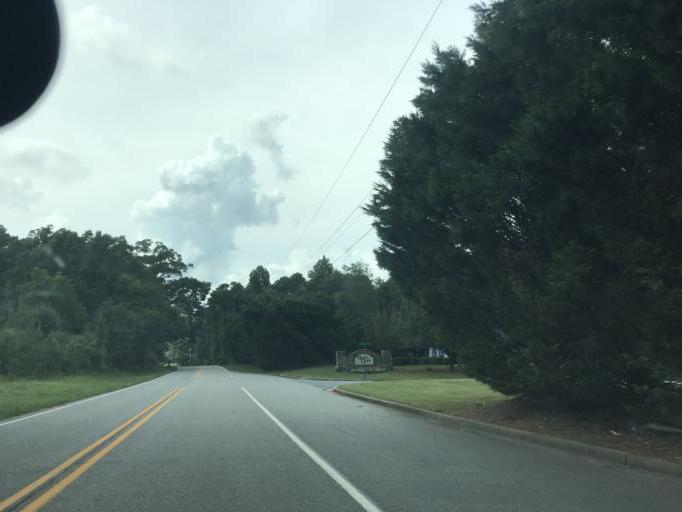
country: US
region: Georgia
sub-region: Forsyth County
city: Cumming
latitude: 34.2130
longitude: -84.2367
